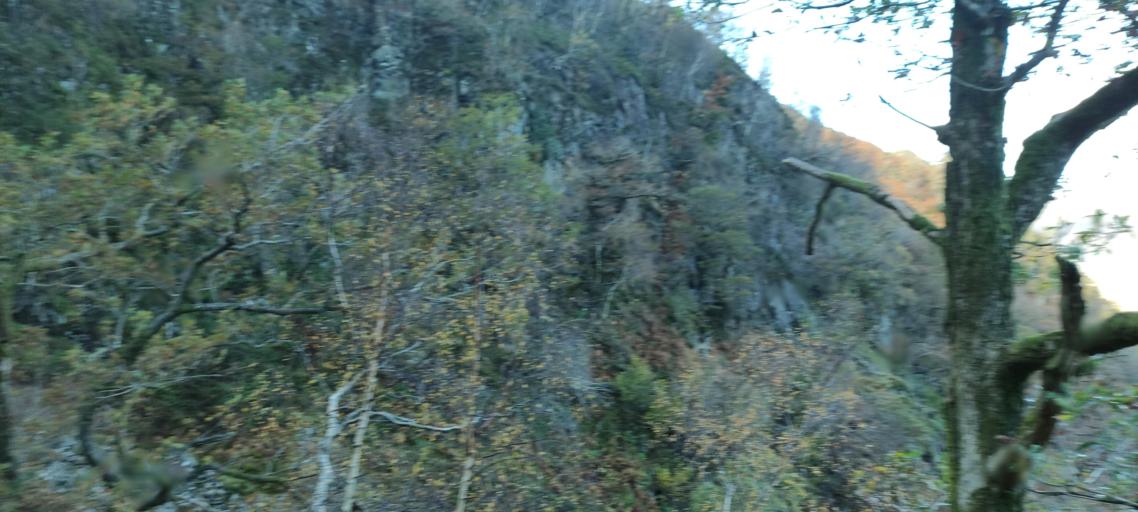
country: GB
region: England
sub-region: Cumbria
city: Keswick
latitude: 54.5068
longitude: -3.1364
